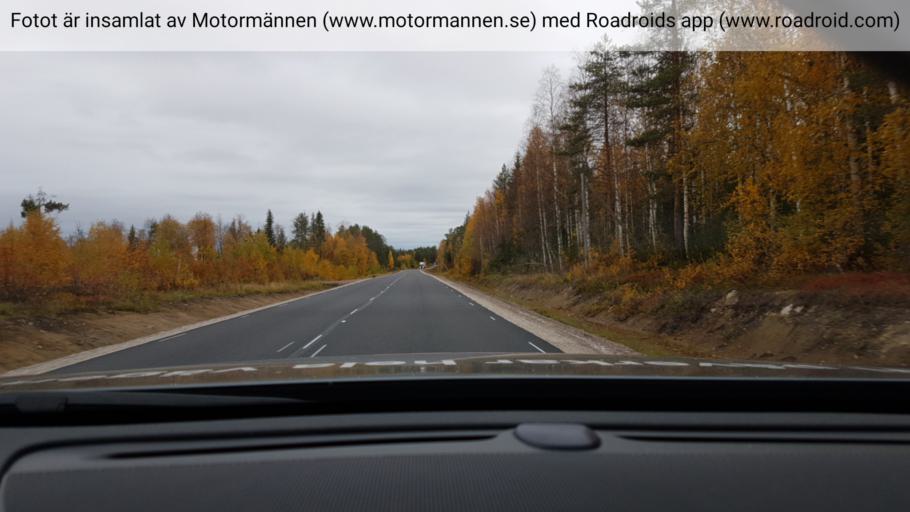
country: SE
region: Norrbotten
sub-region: Overkalix Kommun
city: OEverkalix
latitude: 66.3819
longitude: 22.8309
